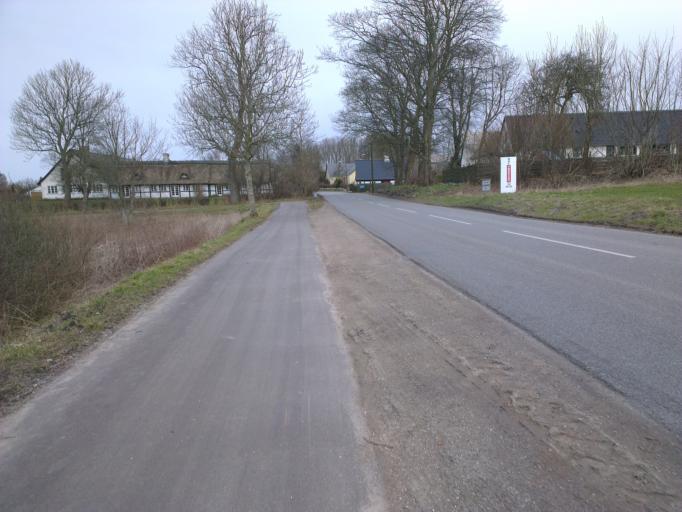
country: DK
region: Capital Region
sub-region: Frederikssund Kommune
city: Skibby
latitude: 55.7739
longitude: 11.9067
